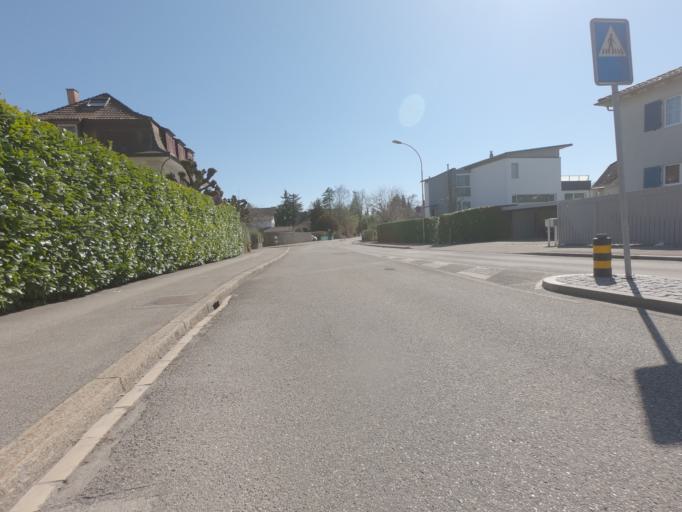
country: CH
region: Solothurn
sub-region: Bezirk Solothurn
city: Solothurn
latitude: 47.2162
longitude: 7.5429
